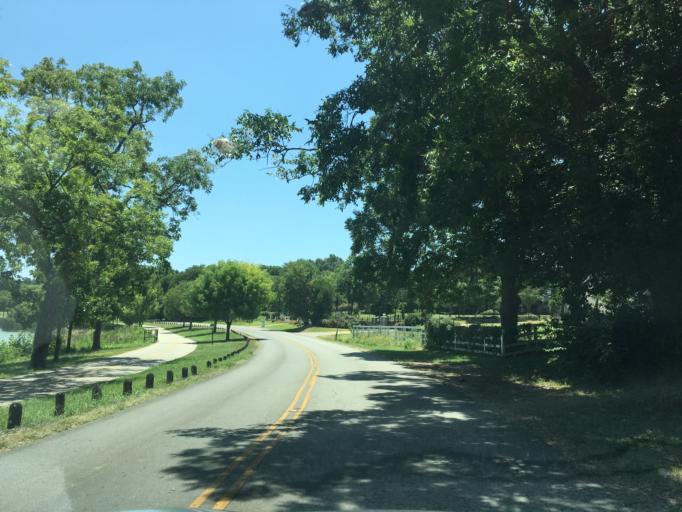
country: US
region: Texas
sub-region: Dallas County
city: Highland Park
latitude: 32.8407
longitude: -96.7301
